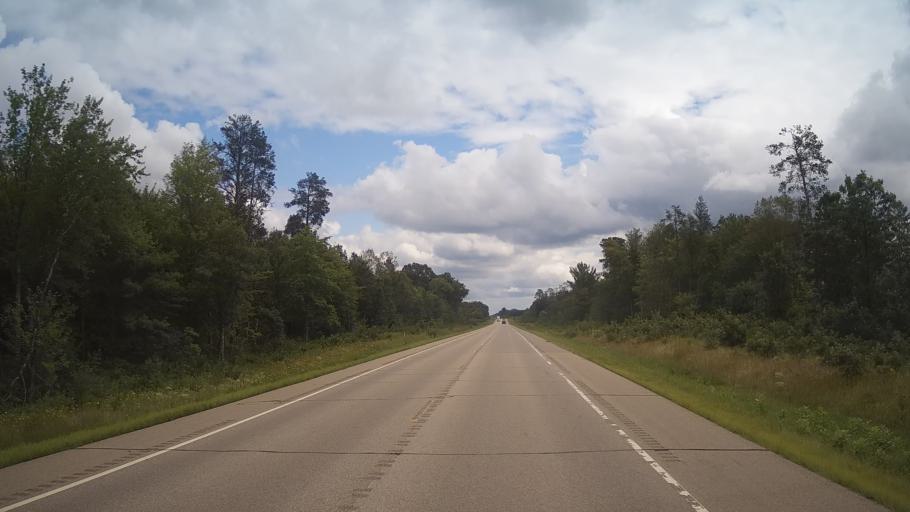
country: US
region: Wisconsin
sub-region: Adams County
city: Friendship
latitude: 44.0251
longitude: -89.7693
